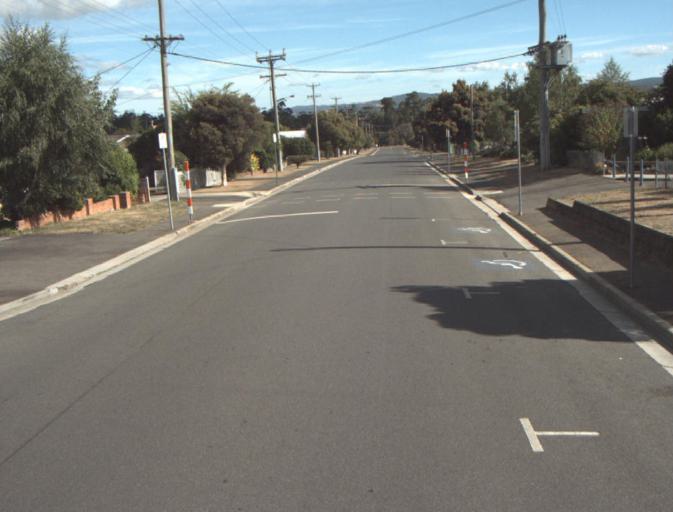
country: AU
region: Tasmania
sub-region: Launceston
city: Newstead
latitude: -41.4629
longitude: 147.1732
